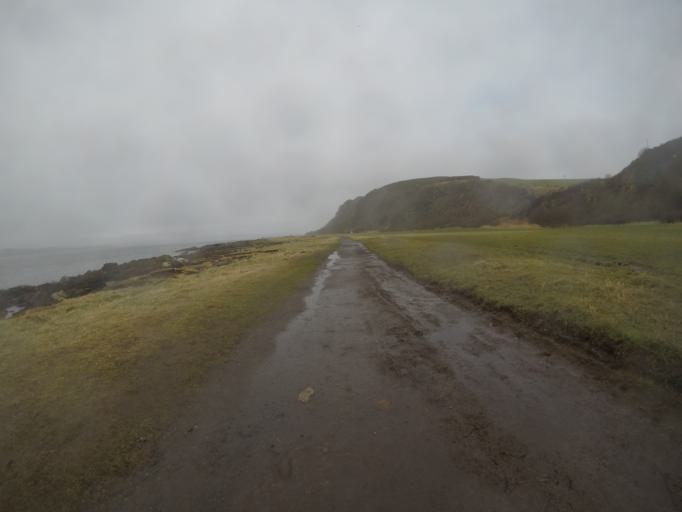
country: GB
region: Scotland
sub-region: North Ayrshire
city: Millport
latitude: 55.7026
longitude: -4.9043
